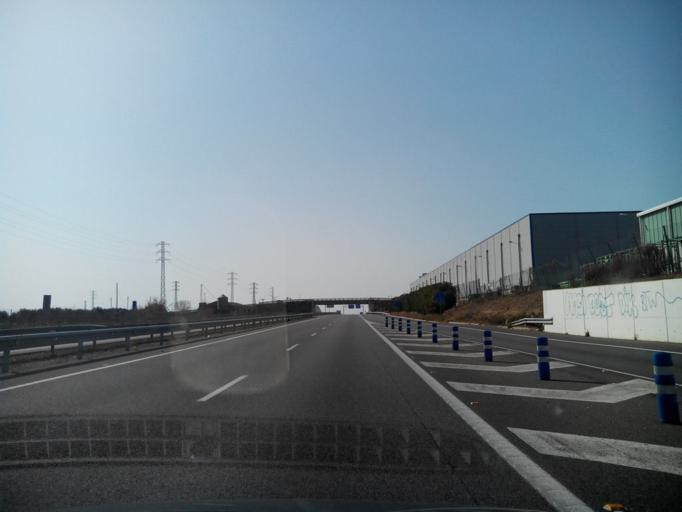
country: ES
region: Catalonia
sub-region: Provincia de Tarragona
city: La Selva
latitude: 41.2177
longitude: 1.1535
